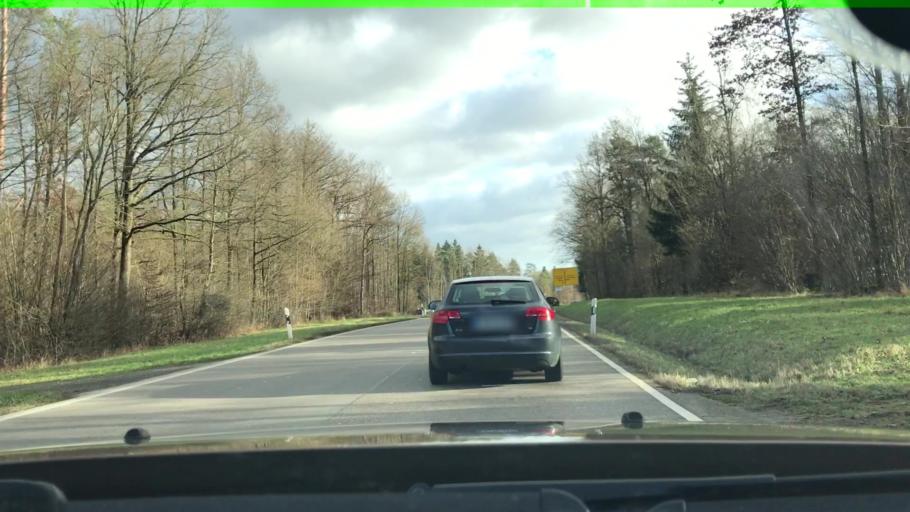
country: DE
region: Baden-Wuerttemberg
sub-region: Regierungsbezirk Stuttgart
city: Kirchberg an der Murr
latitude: 48.9841
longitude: 9.3438
